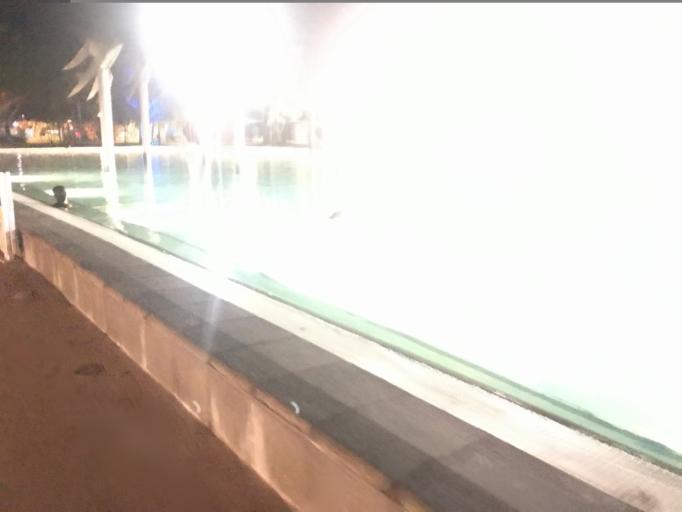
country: AU
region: Queensland
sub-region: Cairns
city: Cairns
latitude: -16.9191
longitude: 145.7780
